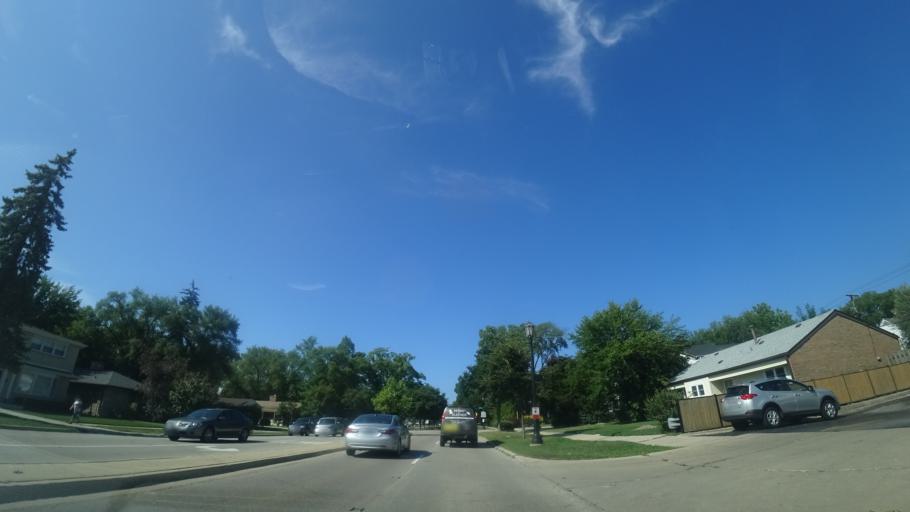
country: US
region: Illinois
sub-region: Cook County
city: Wilmette
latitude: 42.0557
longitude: -87.7274
